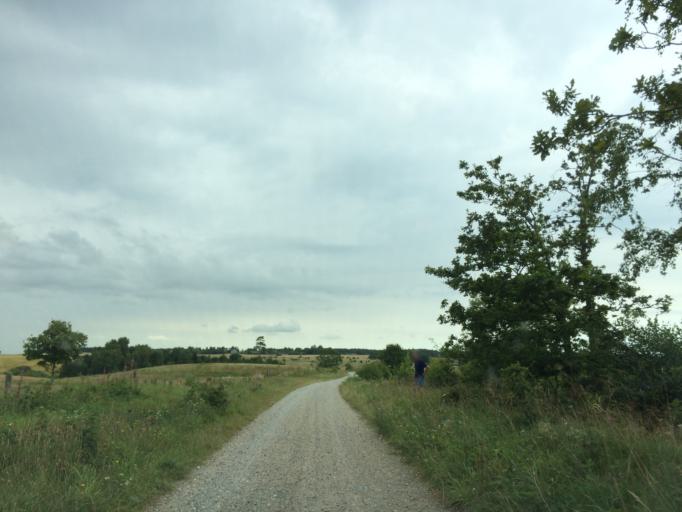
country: DK
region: Central Jutland
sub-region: Syddjurs Kommune
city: Ronde
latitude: 56.2311
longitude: 10.5453
